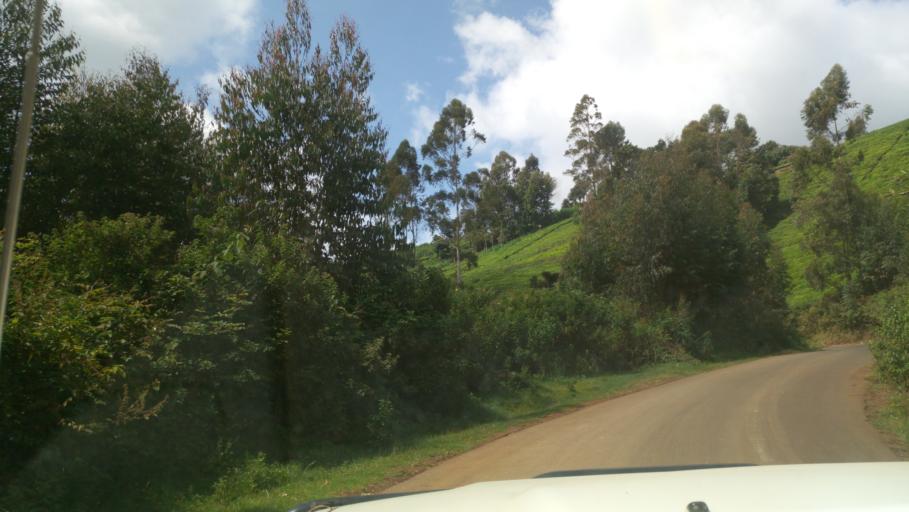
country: KE
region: Murang'a District
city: Kangema
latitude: -0.7681
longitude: 36.8340
